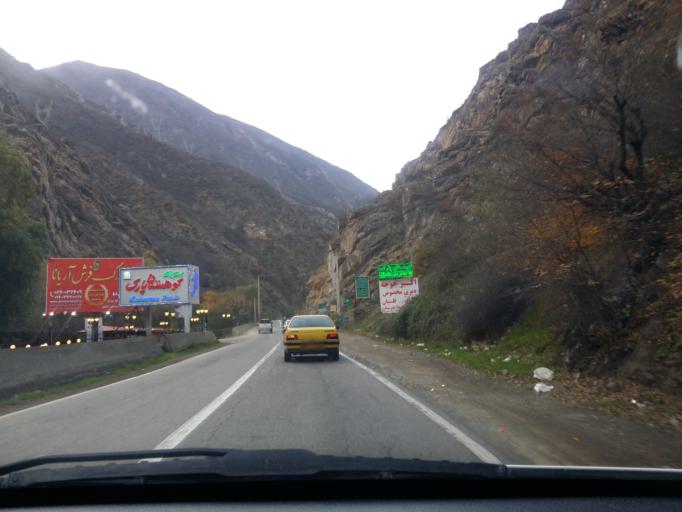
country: IR
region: Mazandaran
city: Chalus
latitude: 36.3143
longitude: 51.2477
